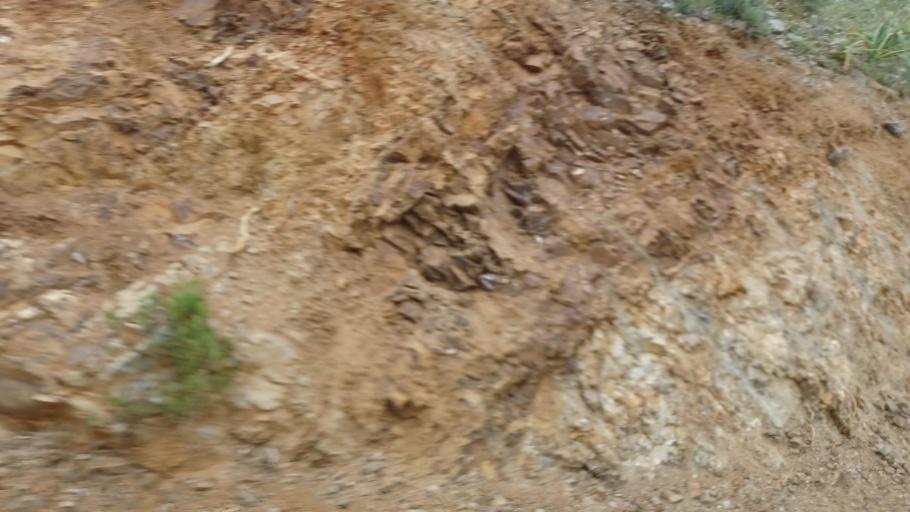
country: CY
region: Limassol
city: Parekklisha
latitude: 34.8366
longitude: 33.1293
